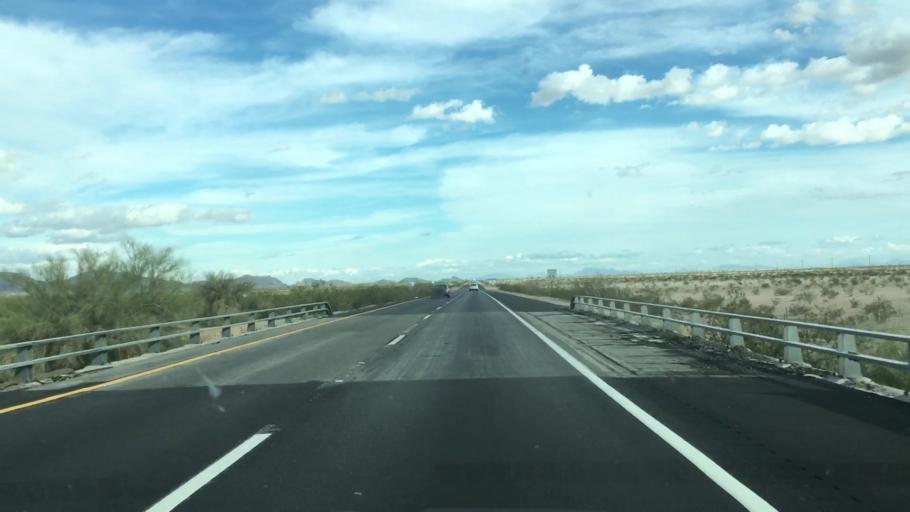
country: US
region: California
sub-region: Riverside County
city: Mesa Verde
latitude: 33.6082
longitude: -114.8826
